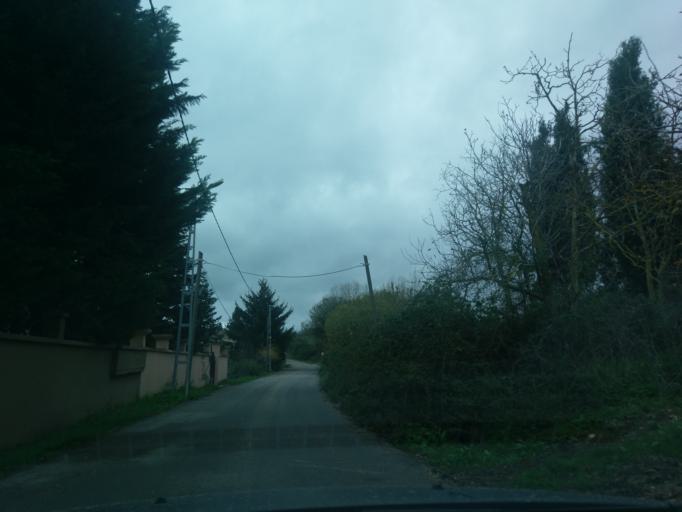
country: TR
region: Istanbul
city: Catalca
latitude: 41.1609
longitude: 28.4419
